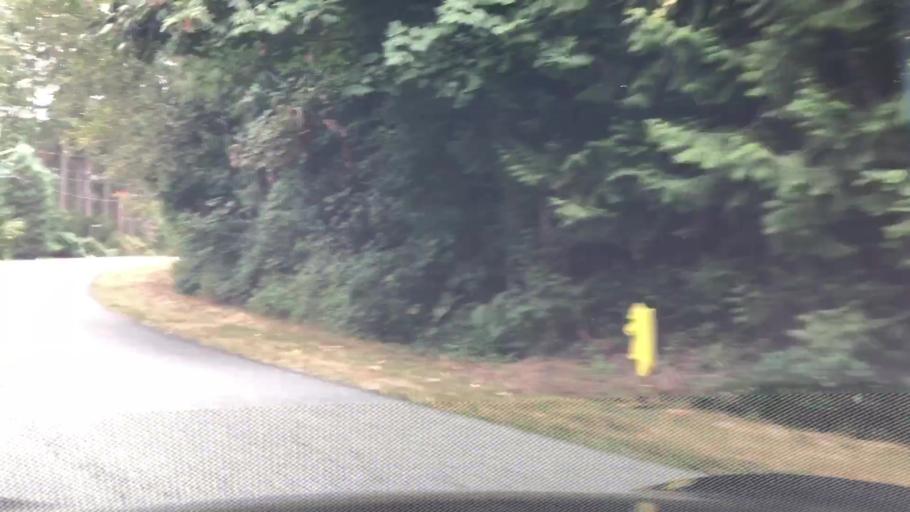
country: US
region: Washington
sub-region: King County
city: Cottage Lake
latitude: 47.7696
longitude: -122.0952
